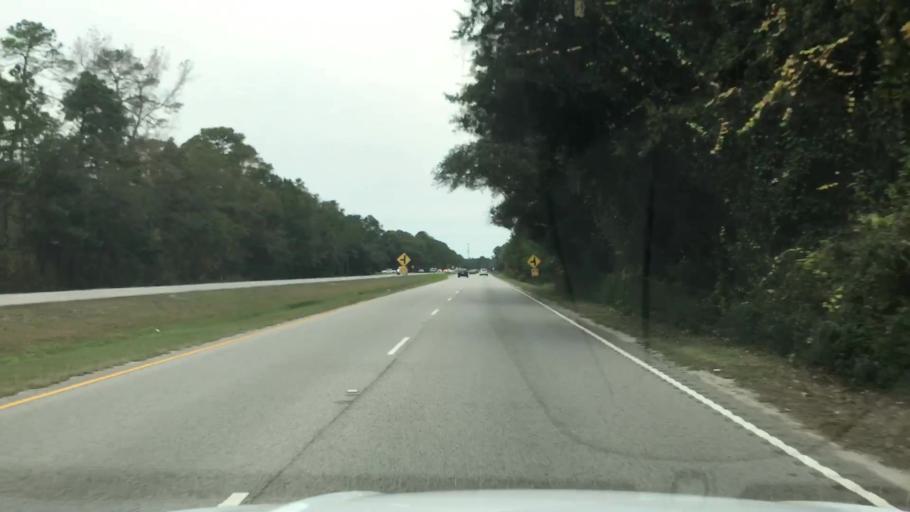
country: US
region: South Carolina
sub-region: Georgetown County
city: Georgetown
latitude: 33.3776
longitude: -79.2121
